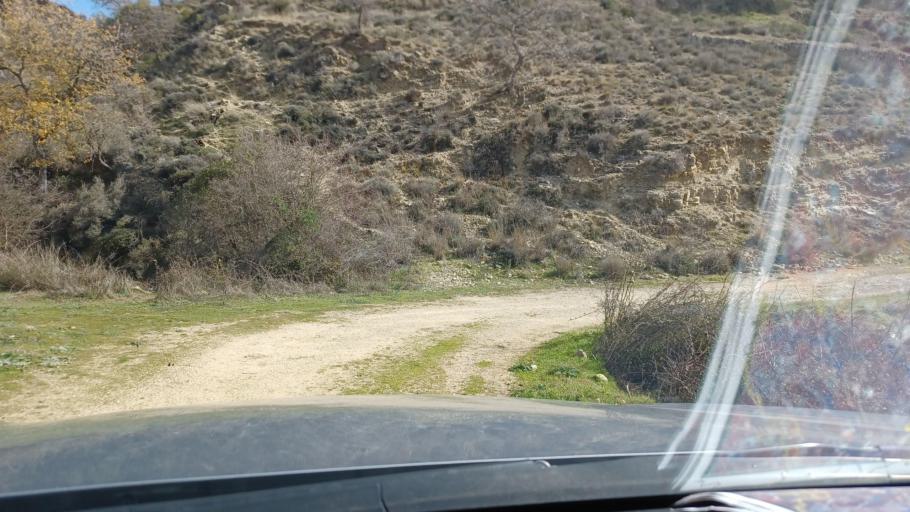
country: CY
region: Limassol
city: Pachna
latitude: 34.8282
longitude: 32.7623
